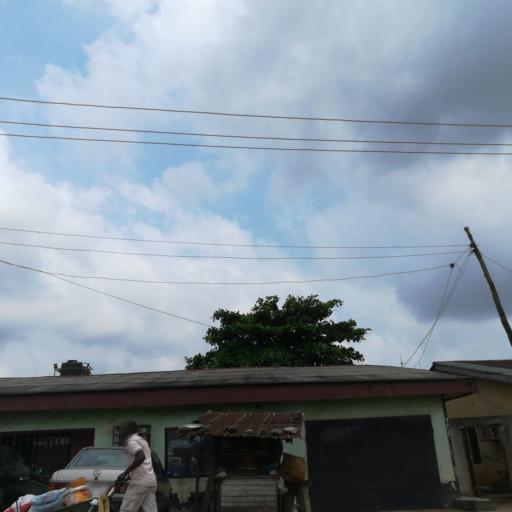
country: NG
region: Rivers
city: Port Harcourt
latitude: 4.8424
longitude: 7.0692
